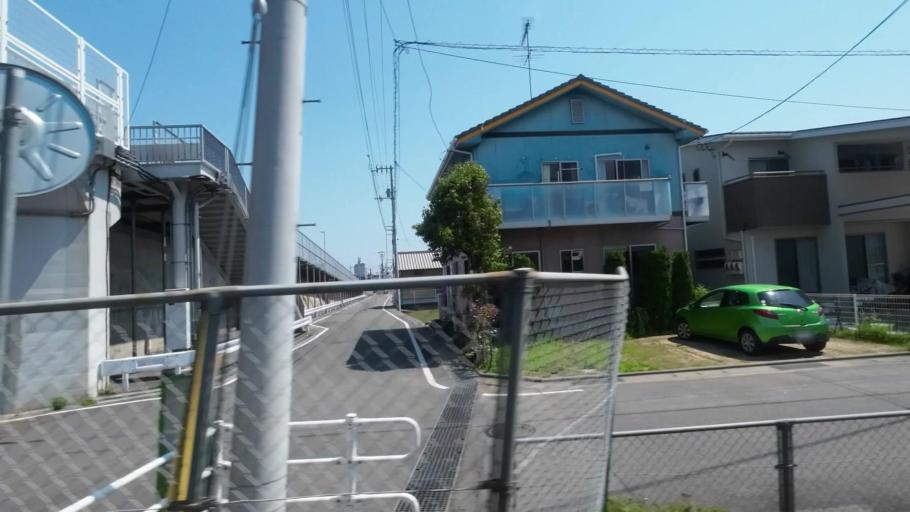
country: JP
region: Ehime
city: Saijo
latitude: 33.9274
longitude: 133.0876
